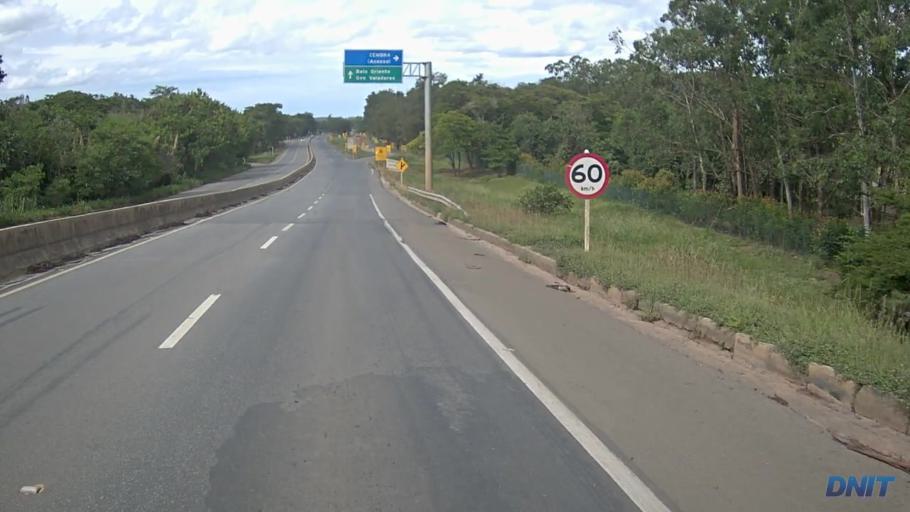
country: BR
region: Minas Gerais
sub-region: Ipaba
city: Ipaba
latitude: -19.3173
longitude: -42.4015
